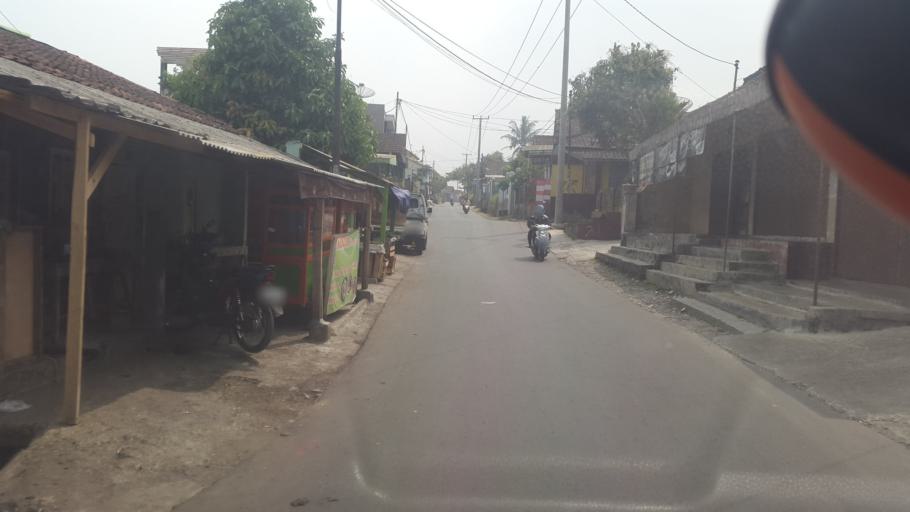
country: ID
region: West Java
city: Sukabumi
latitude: -6.9065
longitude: 106.8979
